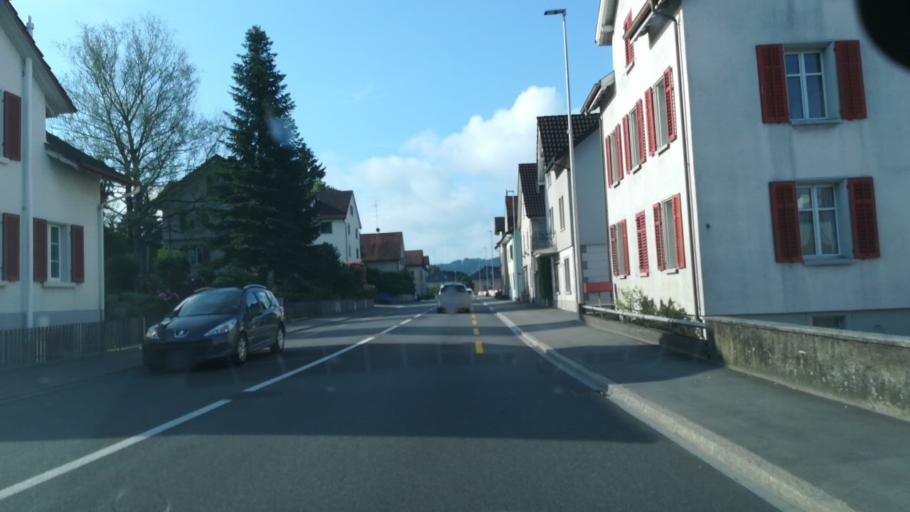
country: CH
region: Thurgau
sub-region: Weinfelden District
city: Sulgen
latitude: 47.5354
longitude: 9.1867
